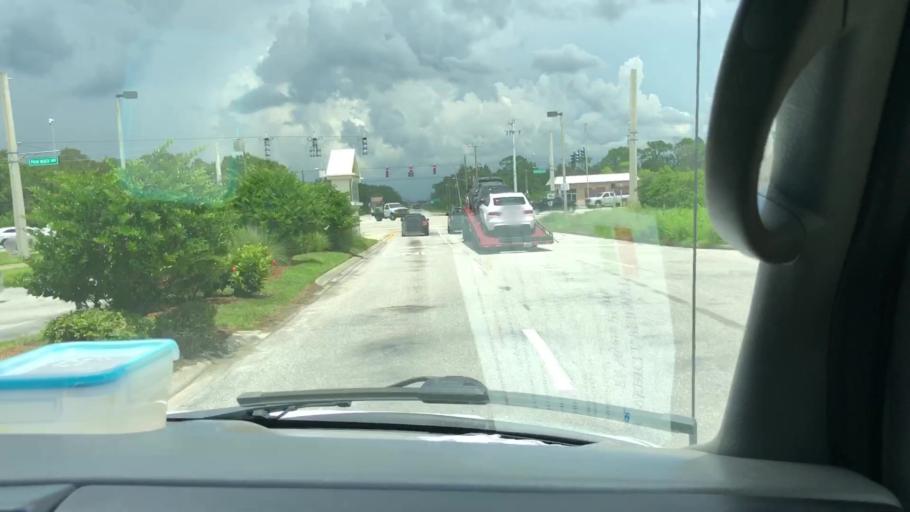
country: US
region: Florida
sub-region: Lee County
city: Fort Myers Shores
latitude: 26.7004
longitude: -81.7601
